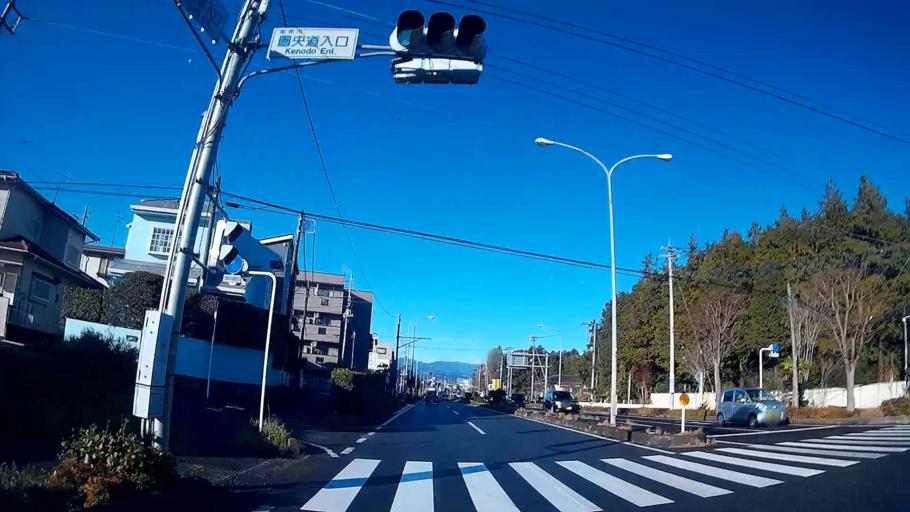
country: JP
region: Saitama
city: Hanno
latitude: 35.8575
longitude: 139.3472
